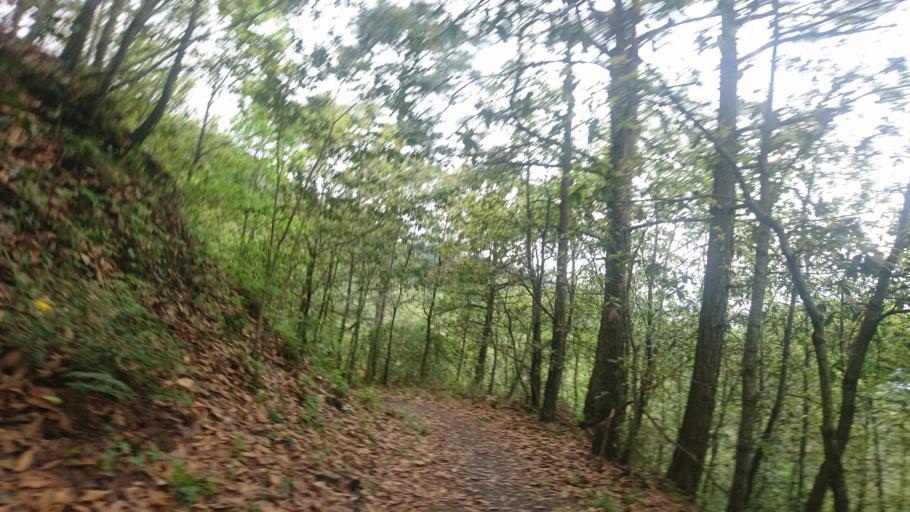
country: MX
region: Nuevo Leon
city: Garza Garcia
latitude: 25.6010
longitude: -100.3382
